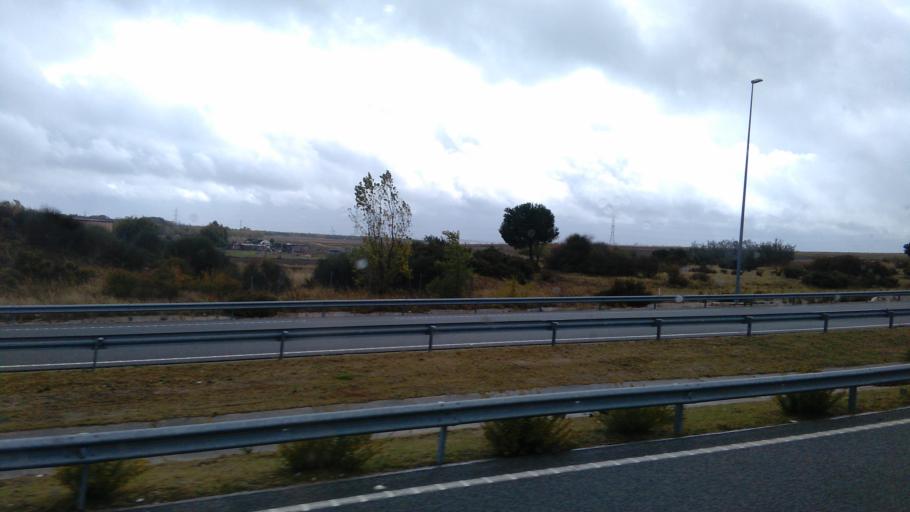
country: ES
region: Madrid
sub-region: Provincia de Madrid
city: Alcorcon
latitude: 40.3331
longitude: -3.8121
